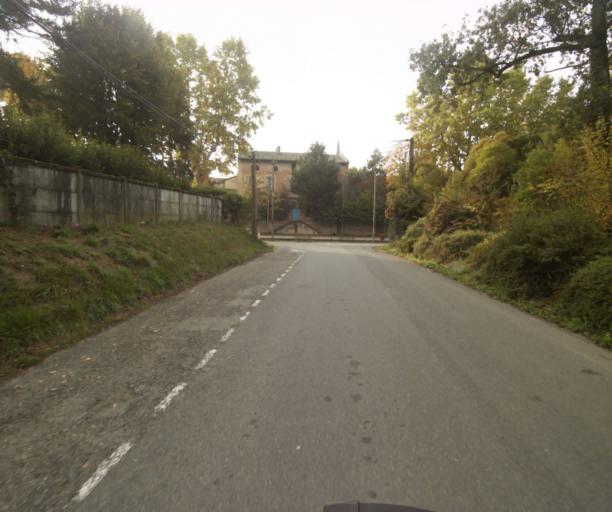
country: FR
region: Midi-Pyrenees
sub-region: Departement du Tarn-et-Garonne
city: Montech
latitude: 43.9589
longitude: 1.2301
